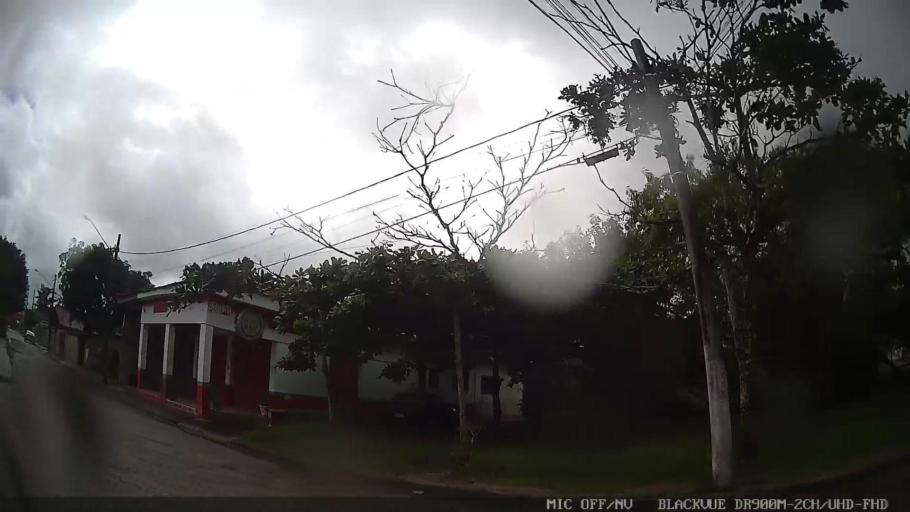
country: BR
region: Sao Paulo
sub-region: Itanhaem
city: Itanhaem
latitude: -24.1911
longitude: -46.8226
